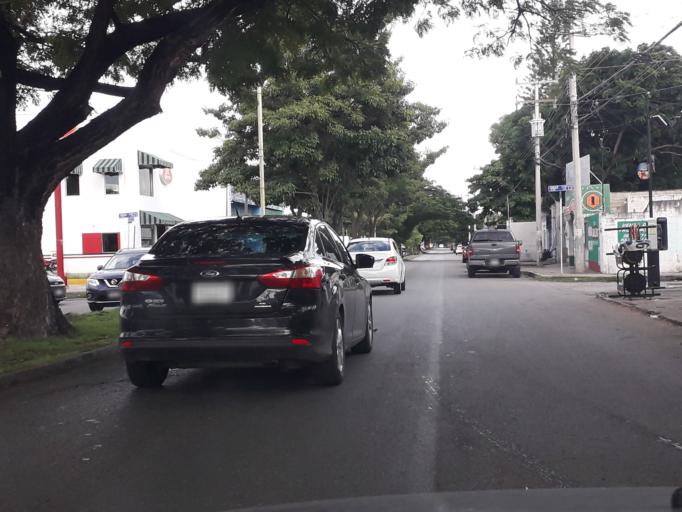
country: MX
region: Yucatan
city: Merida
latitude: 20.9617
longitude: -89.6625
